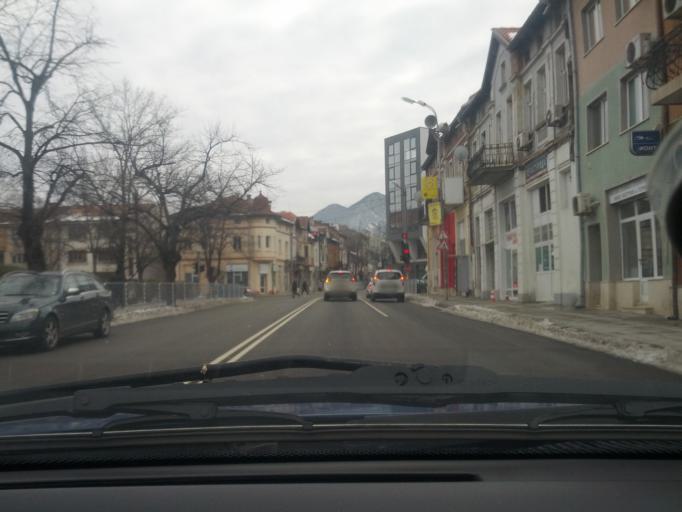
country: BG
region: Vratsa
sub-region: Obshtina Vratsa
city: Vratsa
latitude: 43.2082
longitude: 23.5465
